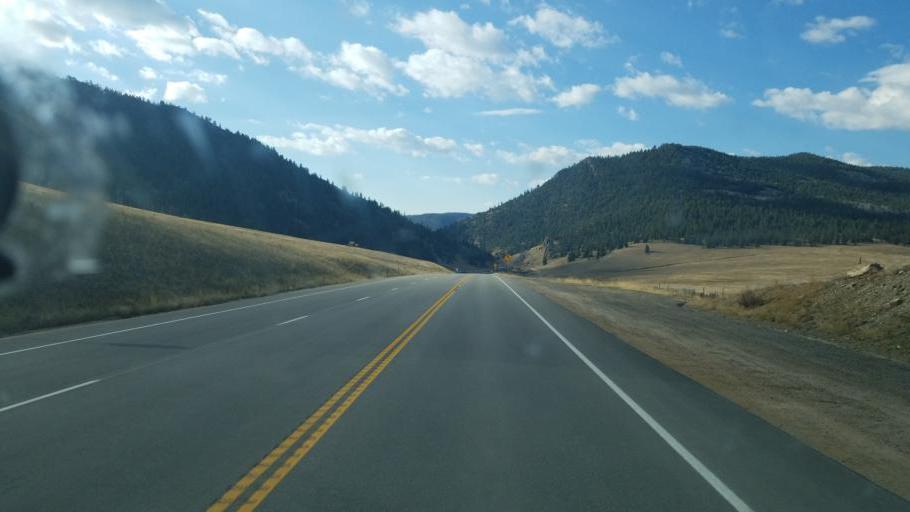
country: US
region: Colorado
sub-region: Chaffee County
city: Buena Vista
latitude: 38.8703
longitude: -105.9845
